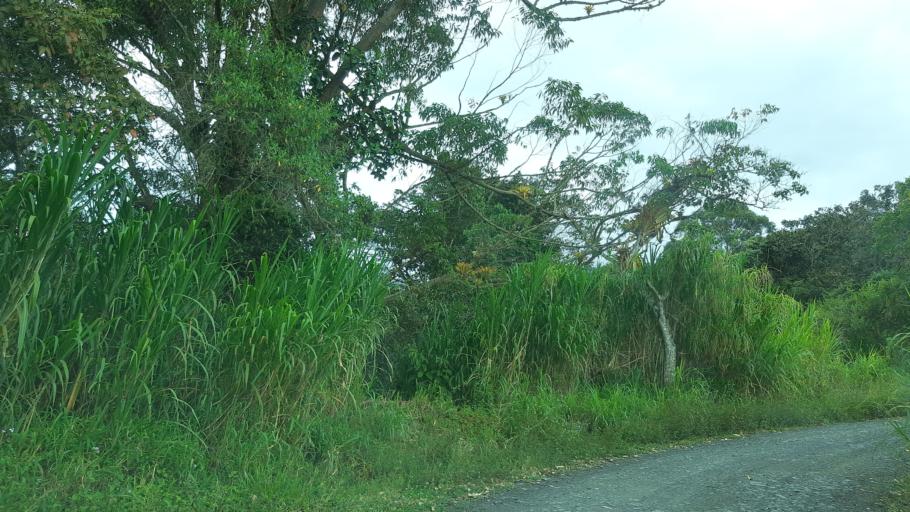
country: CO
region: Boyaca
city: Garagoa
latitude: 5.0184
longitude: -73.3316
